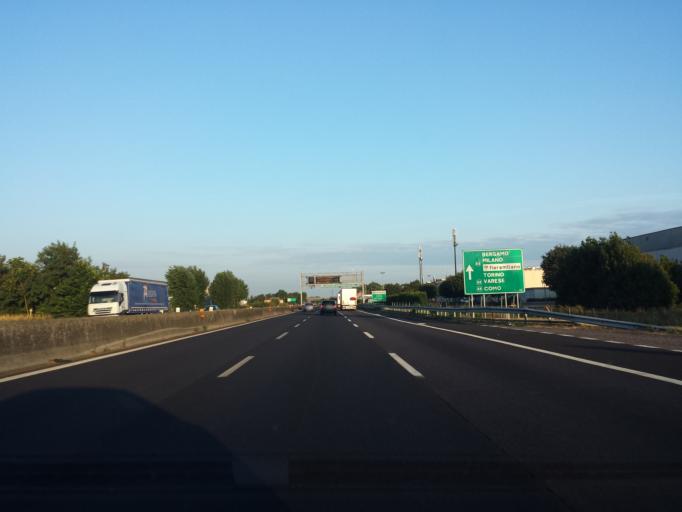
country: IT
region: Lombardy
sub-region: Provincia di Brescia
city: Folzano
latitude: 45.5198
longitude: 10.1885
